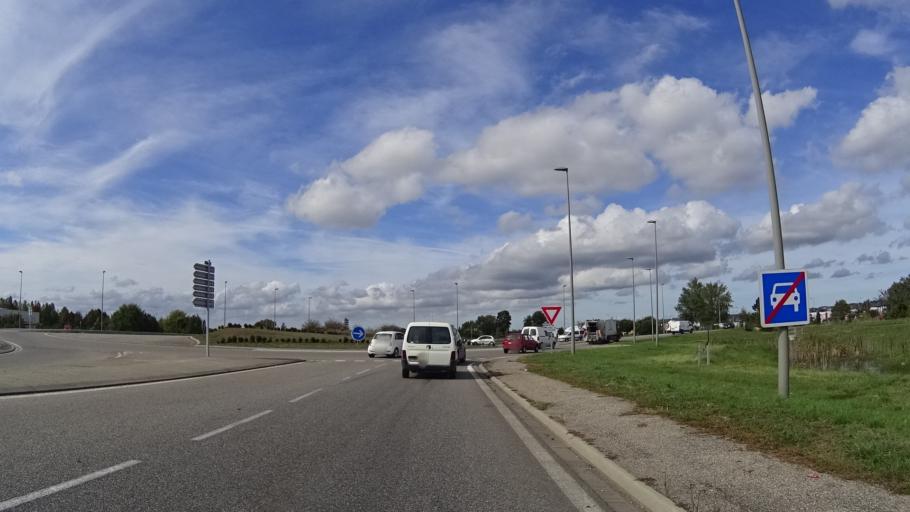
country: FR
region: Aquitaine
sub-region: Departement du Lot-et-Garonne
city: Bon-Encontre
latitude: 44.1734
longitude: 0.6584
